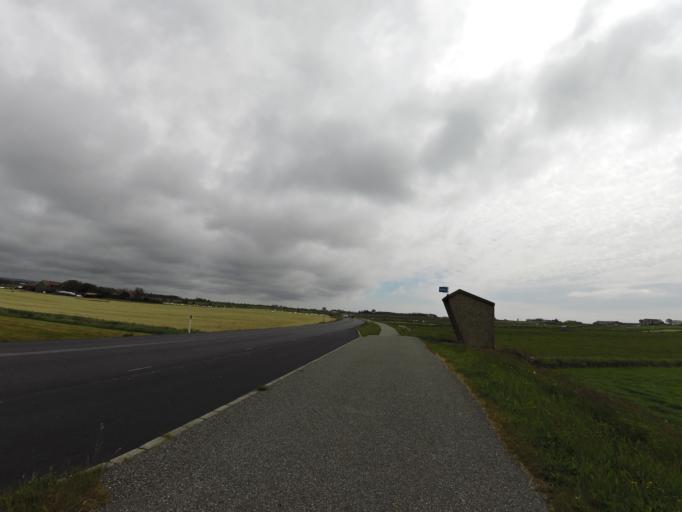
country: NO
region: Rogaland
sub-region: Ha
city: Naerbo
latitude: 58.6505
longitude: 5.6004
